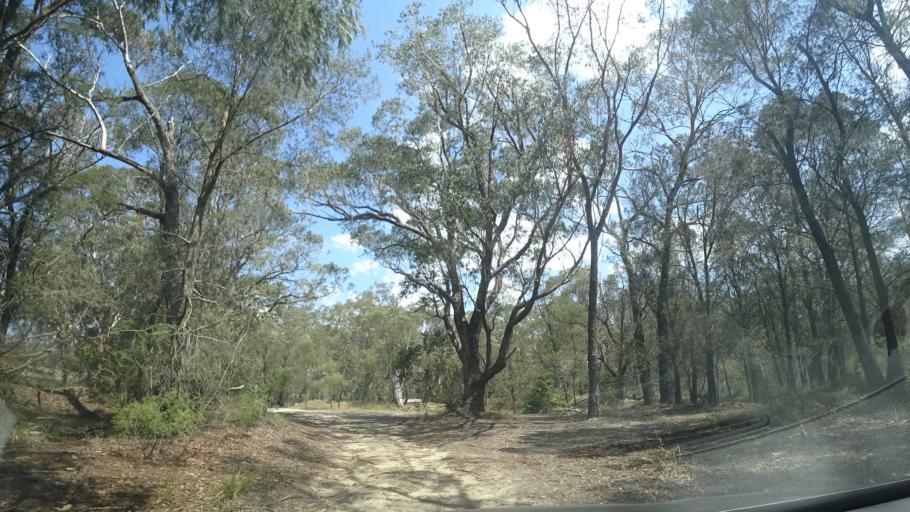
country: AU
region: New South Wales
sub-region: Wingecarribee
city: Bundanoon
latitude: -34.6382
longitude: 150.2549
